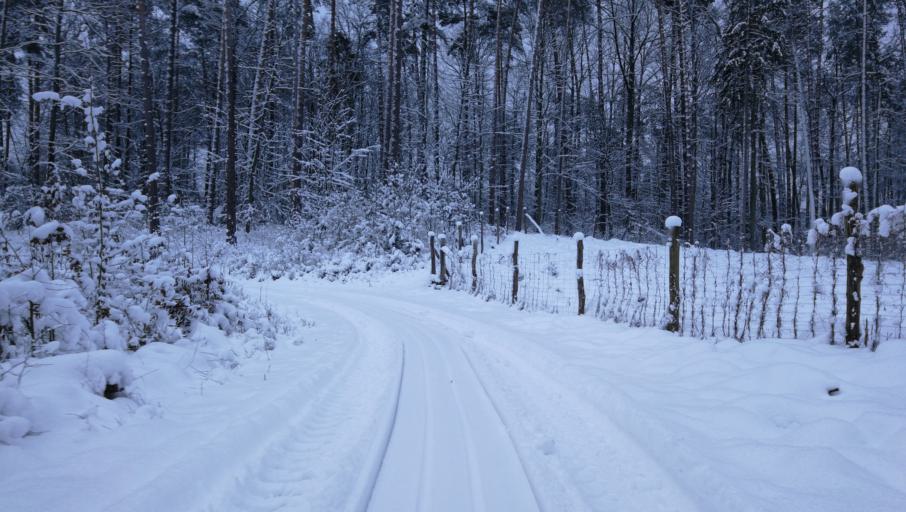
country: PL
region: Kujawsko-Pomorskie
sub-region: Powiat brodnicki
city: Gorzno
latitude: 53.2086
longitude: 19.6945
